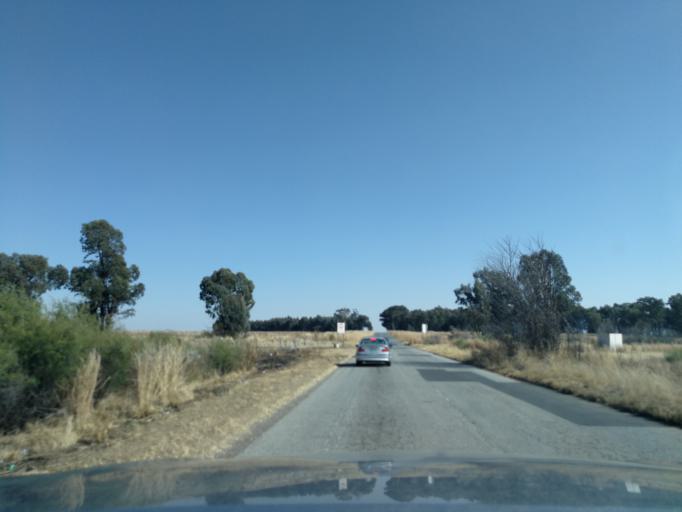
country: ZA
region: North-West
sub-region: Dr Kenneth Kaunda District Municipality
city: Orkney
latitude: -27.0514
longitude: 26.7272
